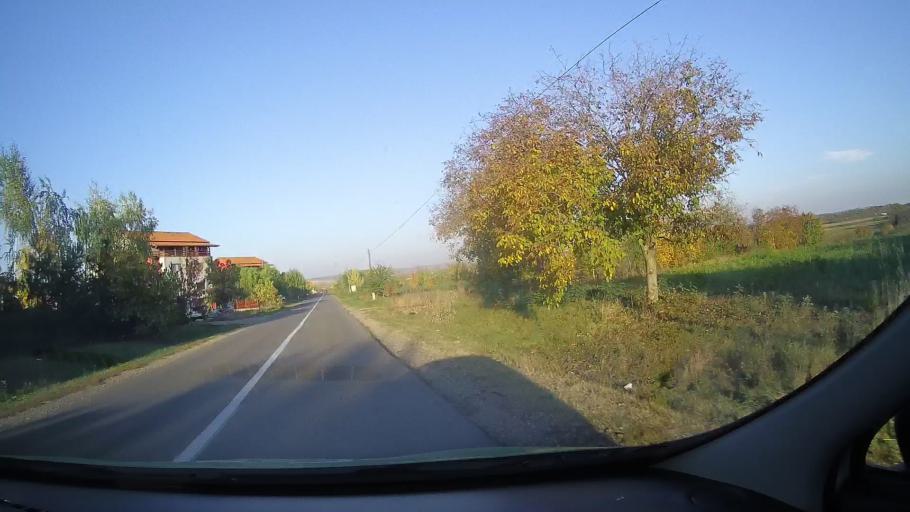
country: RO
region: Bihor
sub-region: Comuna Paleu
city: Paleu
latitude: 47.1105
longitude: 21.9351
